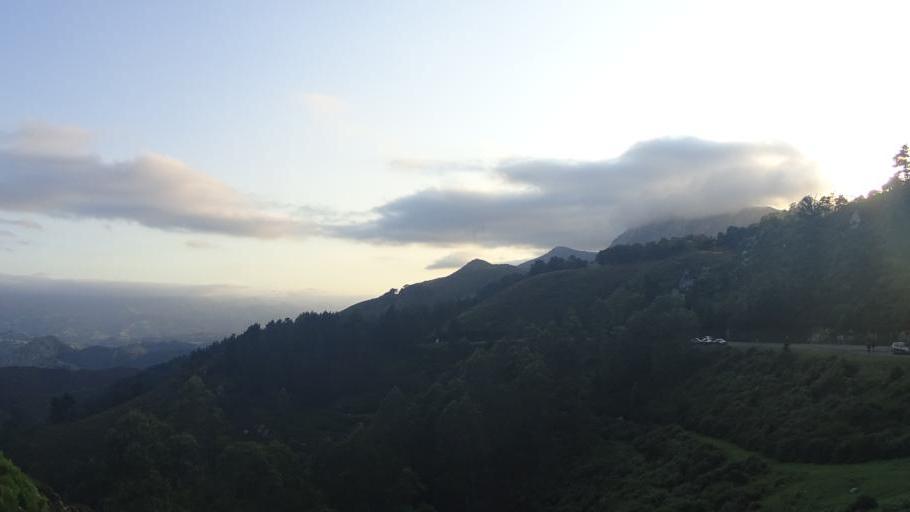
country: ES
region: Asturias
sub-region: Province of Asturias
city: Colunga
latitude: 43.4387
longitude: -5.1929
